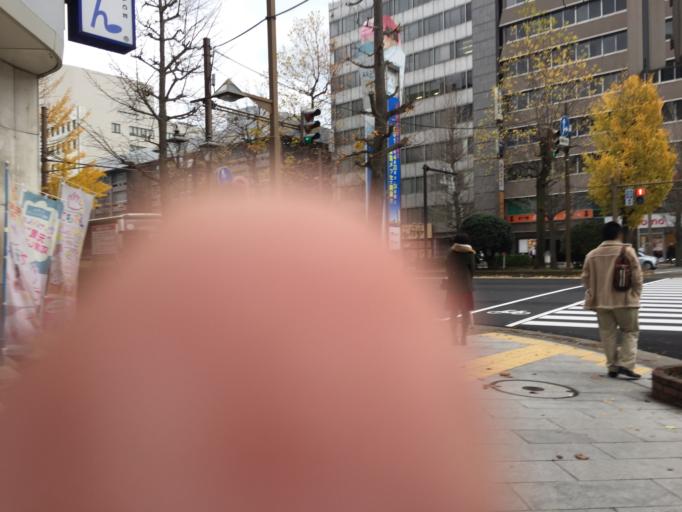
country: JP
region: Niigata
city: Niigata-shi
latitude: 37.9133
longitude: 139.0608
